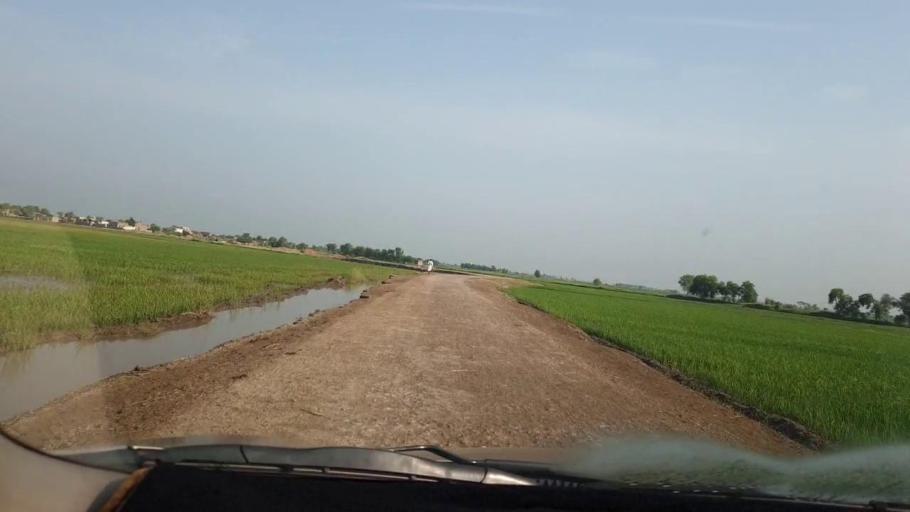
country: PK
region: Sindh
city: Goth Garelo
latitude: 27.4845
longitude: 68.0709
